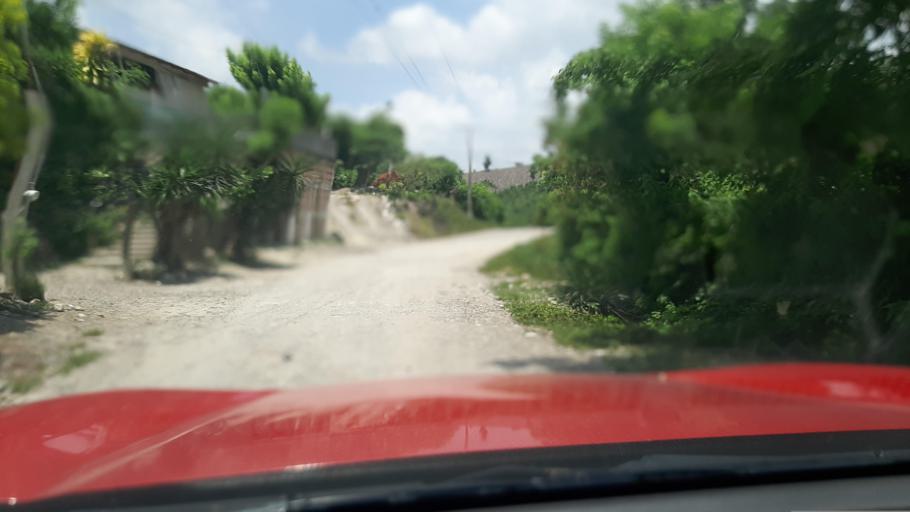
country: MX
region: Veracruz
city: Papantla de Olarte
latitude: 20.4344
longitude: -97.2648
